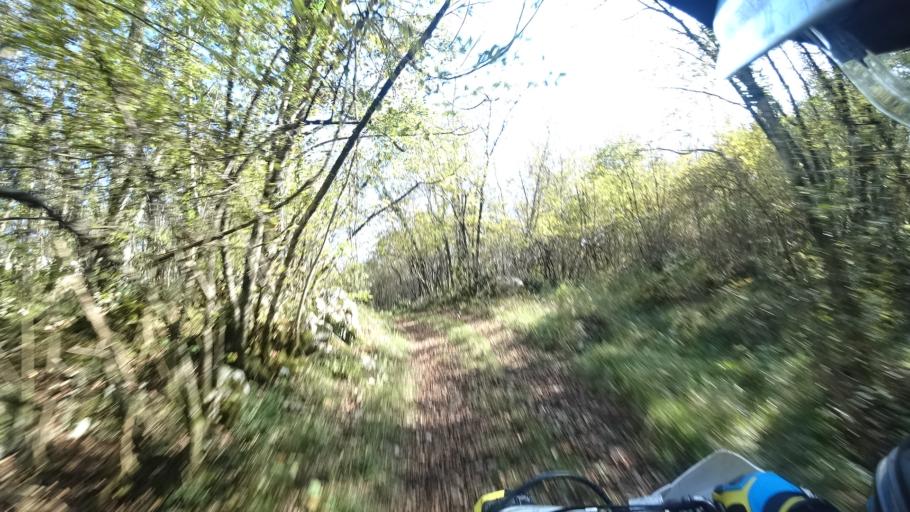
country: HR
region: Primorsko-Goranska
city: Matulji
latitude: 45.3909
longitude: 14.2961
